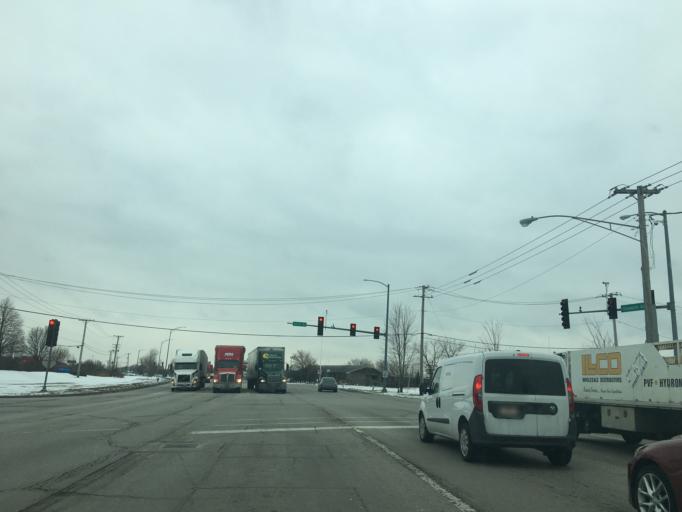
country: US
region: Illinois
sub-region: Kane County
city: North Aurora
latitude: 41.8069
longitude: -88.2816
